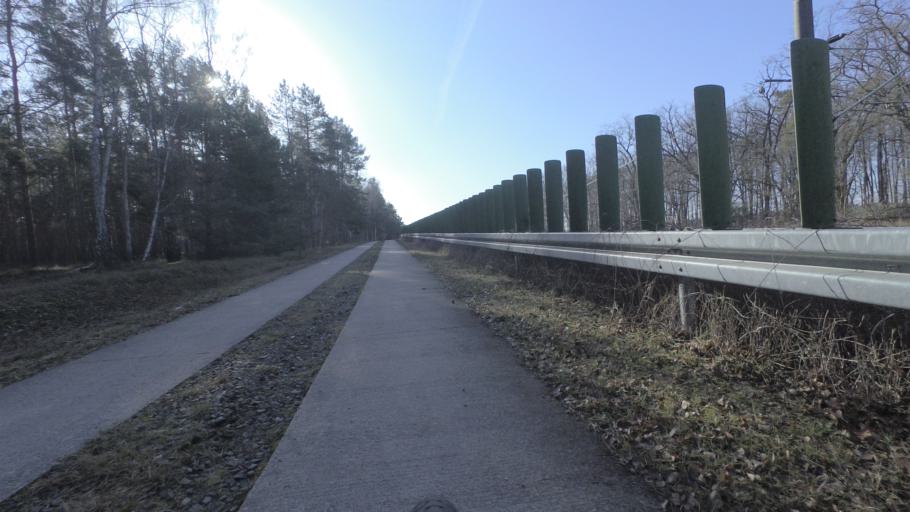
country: DE
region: Brandenburg
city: Trebbin
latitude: 52.1466
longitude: 13.2194
